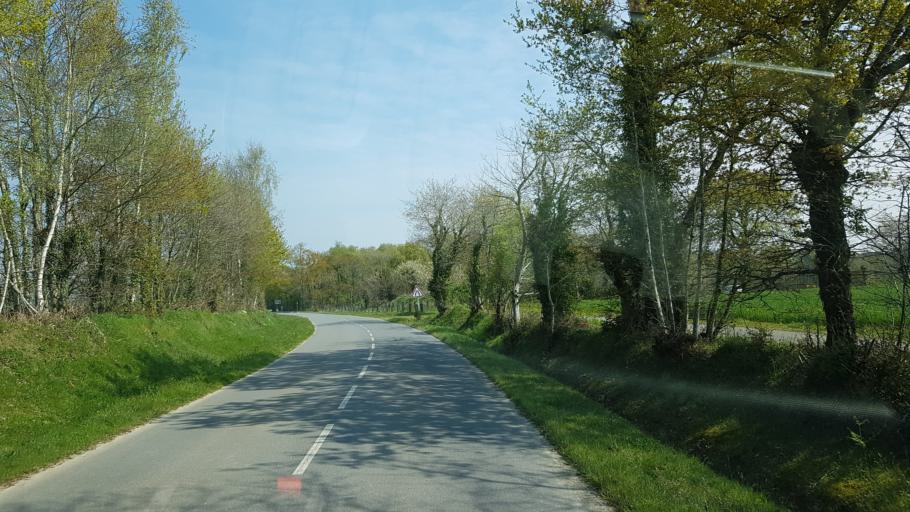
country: FR
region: Brittany
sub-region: Departement du Morbihan
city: Peaule
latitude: 47.5892
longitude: -2.4041
